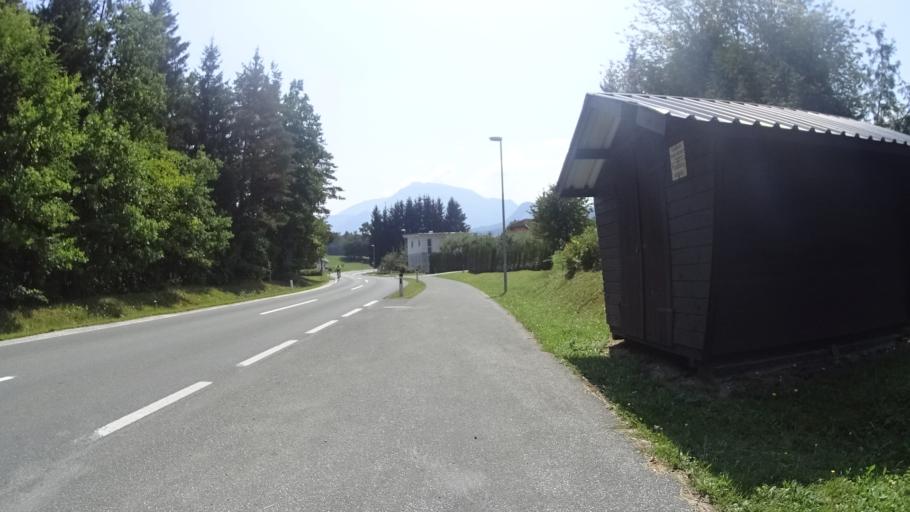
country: AT
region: Carinthia
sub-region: Politischer Bezirk Volkermarkt
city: Eberndorf
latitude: 46.5738
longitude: 14.6588
